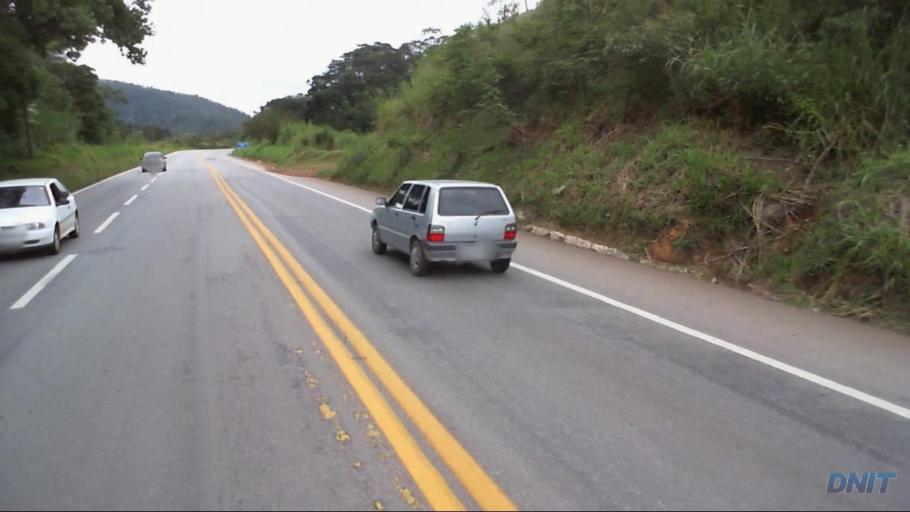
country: BR
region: Minas Gerais
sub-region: Joao Monlevade
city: Joao Monlevade
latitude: -19.8495
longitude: -43.1572
